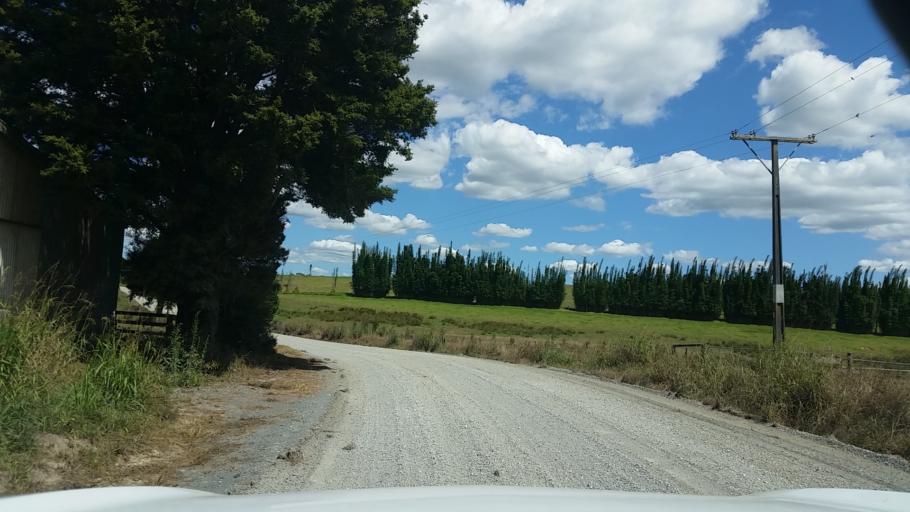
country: NZ
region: Northland
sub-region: Whangarei
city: Maungatapere
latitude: -35.6915
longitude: 174.1437
